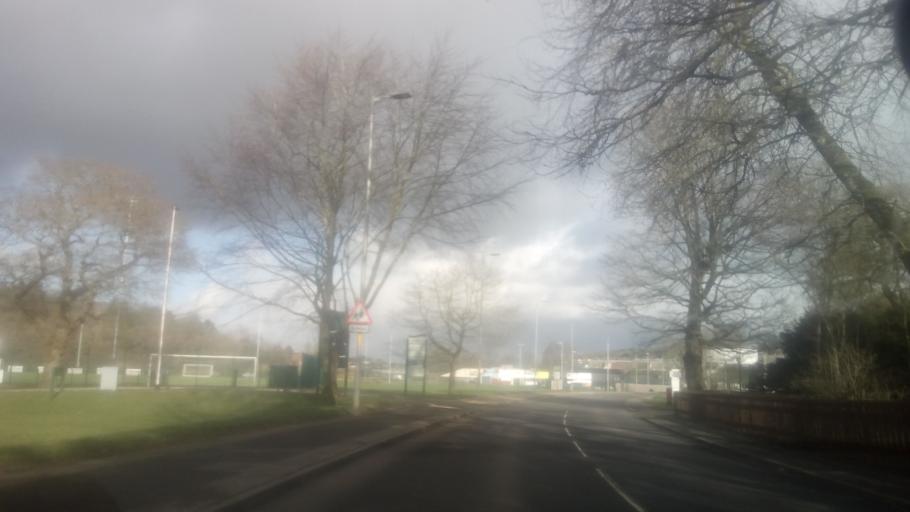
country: GB
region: Scotland
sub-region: The Scottish Borders
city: Hawick
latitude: 55.4207
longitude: -2.7996
